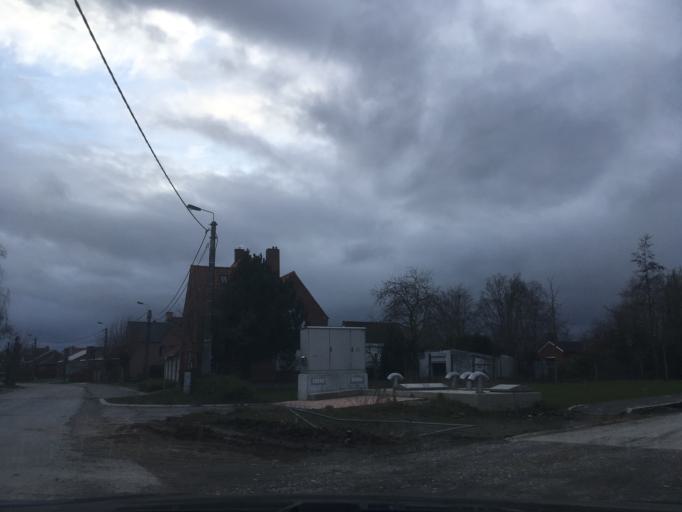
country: BE
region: Flanders
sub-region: Provincie West-Vlaanderen
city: Oostrozebeke
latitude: 50.9011
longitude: 3.3352
